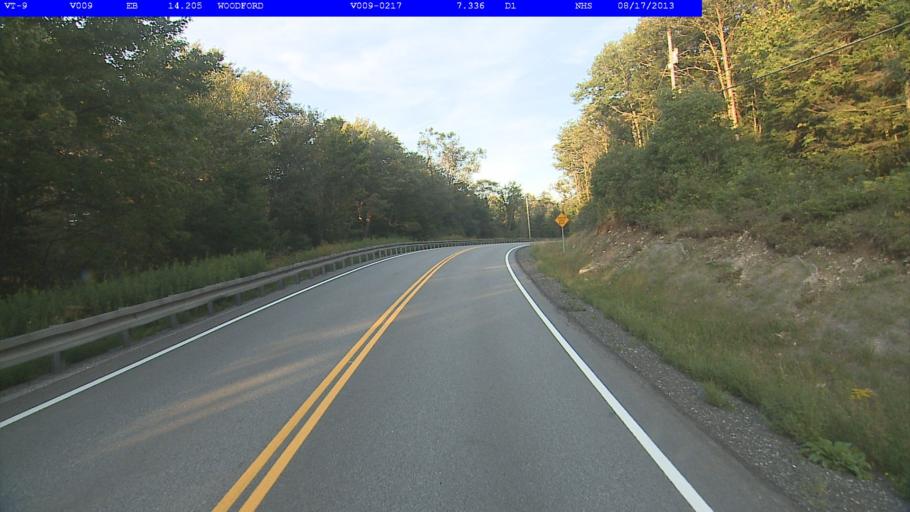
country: US
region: Vermont
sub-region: Bennington County
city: Bennington
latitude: 42.8985
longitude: -73.0506
